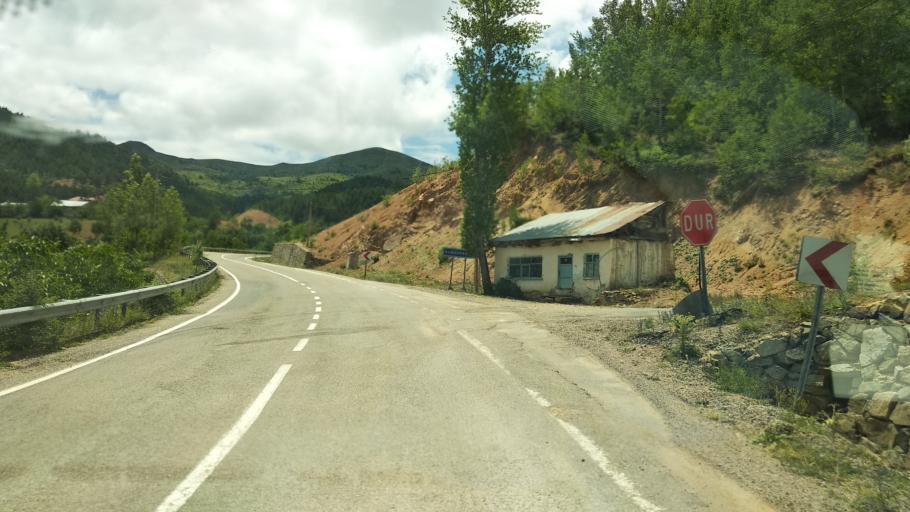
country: TR
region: Gumushane
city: Kose
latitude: 40.3051
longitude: 39.5571
